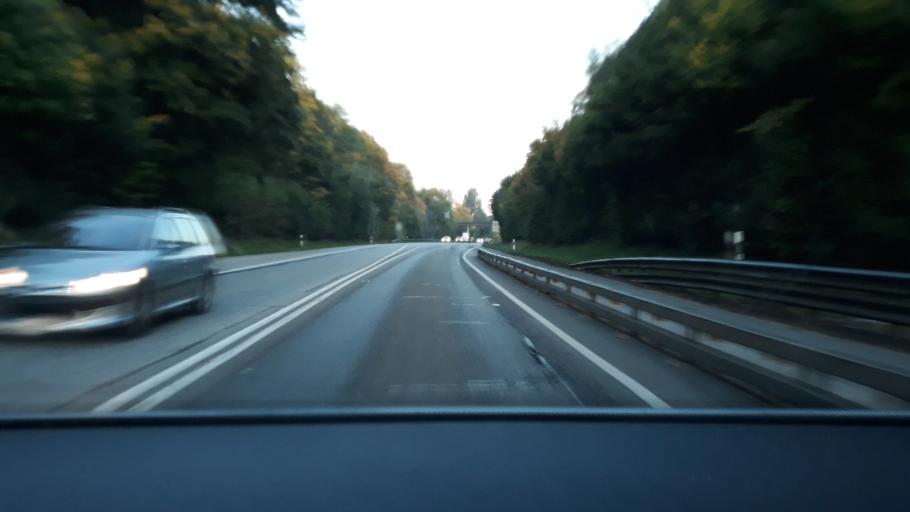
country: DE
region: Schleswig-Holstein
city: Busdorf
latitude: 54.5112
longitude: 9.5188
